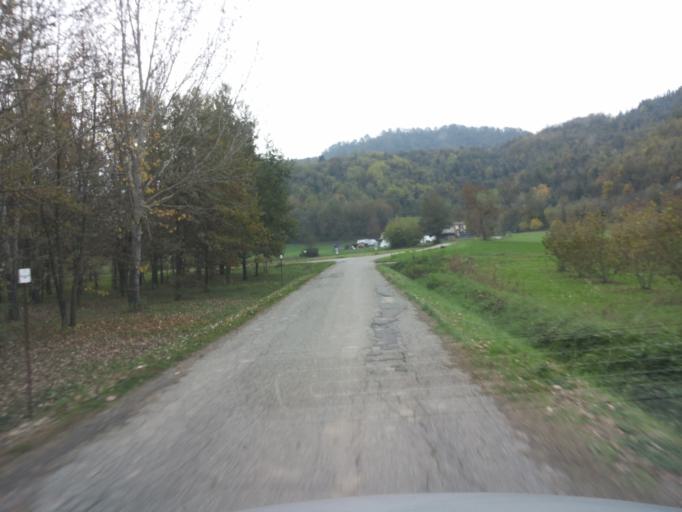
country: IT
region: Piedmont
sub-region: Provincia di Alessandria
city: Serralunga di Crea
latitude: 45.1086
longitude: 8.2734
